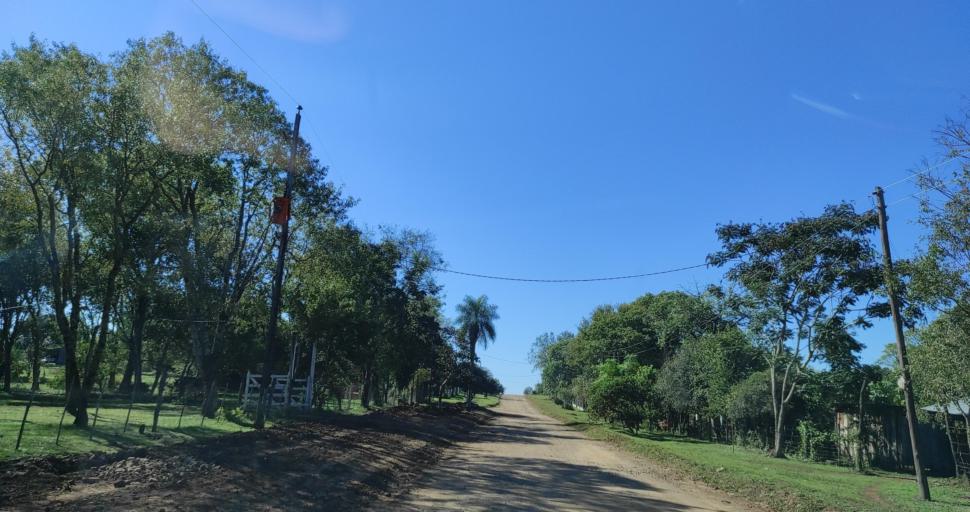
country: AR
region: Misiones
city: Cerro Cora
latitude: -27.5638
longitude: -55.7044
